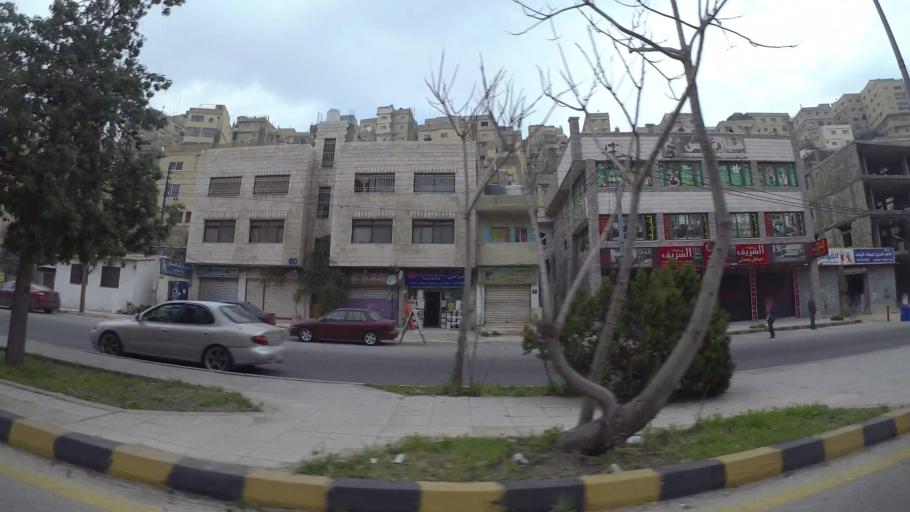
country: JO
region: Amman
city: Amman
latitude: 31.9563
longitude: 35.9393
